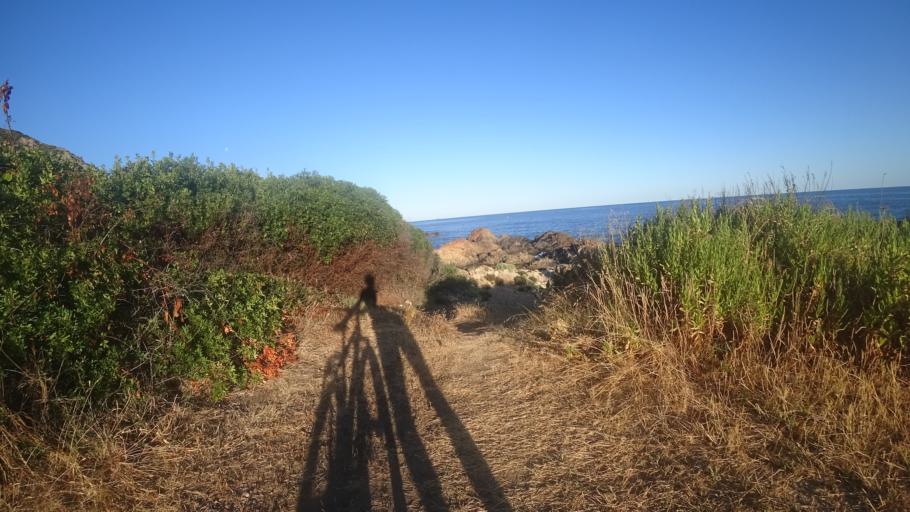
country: FR
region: Corsica
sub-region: Departement de la Corse-du-Sud
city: Alata
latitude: 41.9757
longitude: 8.6610
